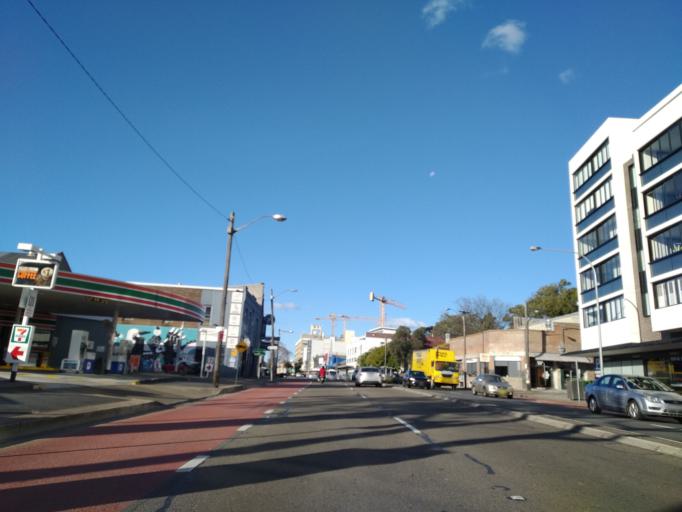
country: AU
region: New South Wales
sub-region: Marrickville
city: Camperdown
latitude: -33.8873
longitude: 151.1739
